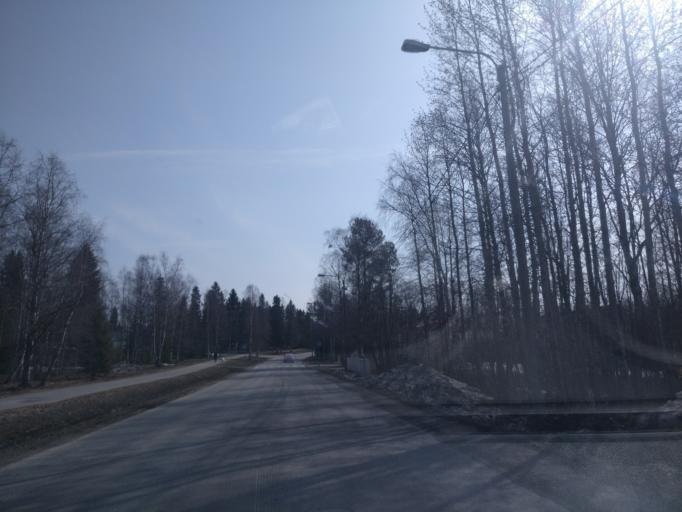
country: FI
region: Lapland
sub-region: Kemi-Tornio
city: Kemi
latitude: 65.7264
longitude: 24.6180
